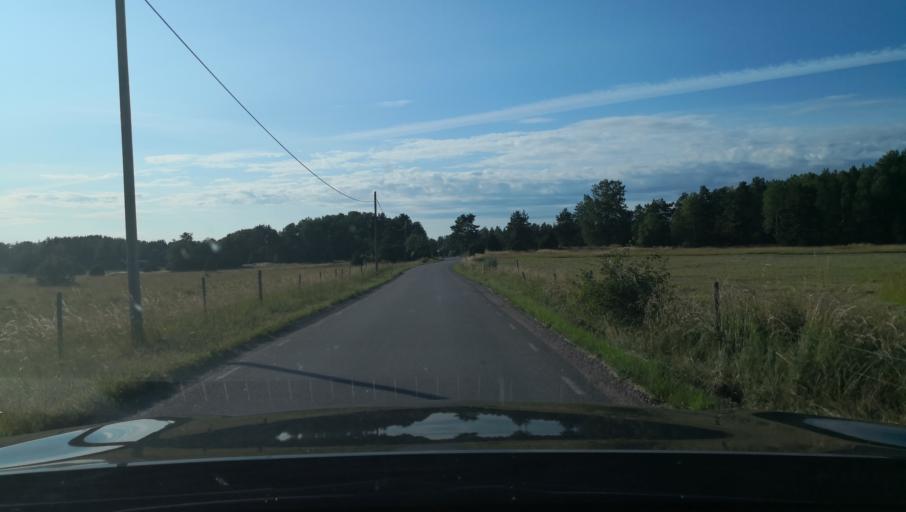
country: SE
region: Uppsala
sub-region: Uppsala Kommun
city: Vattholma
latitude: 59.9280
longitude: 17.8360
